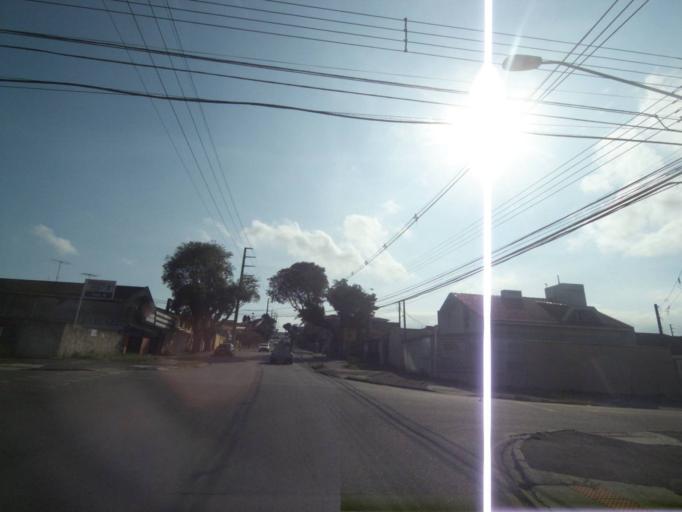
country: BR
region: Parana
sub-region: Pinhais
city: Pinhais
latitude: -25.4064
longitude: -49.2065
